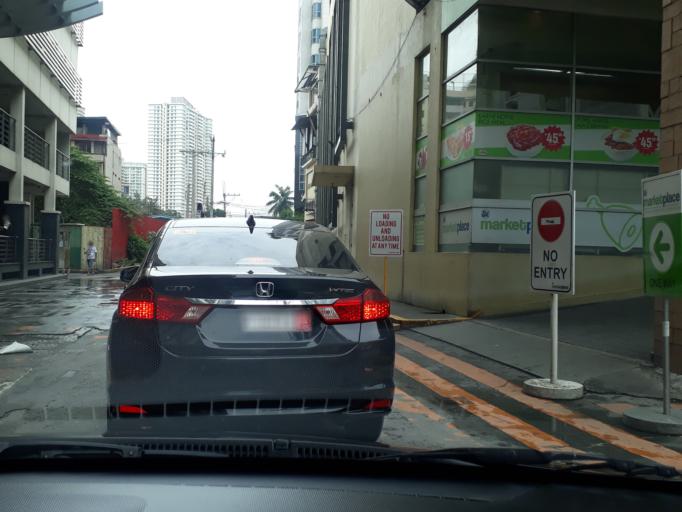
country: PH
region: Metro Manila
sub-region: Makati City
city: Makati City
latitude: 14.5659
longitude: 121.0291
